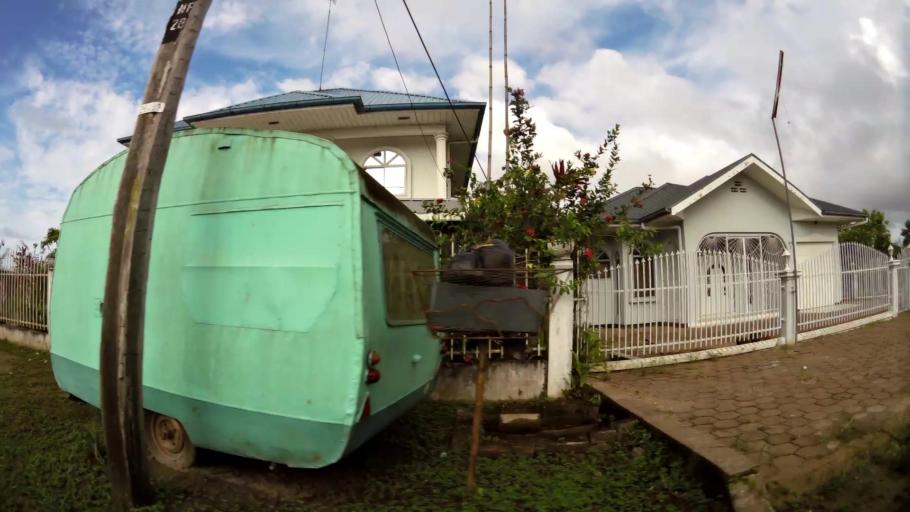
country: SR
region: Paramaribo
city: Paramaribo
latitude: 5.8533
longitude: -55.2313
